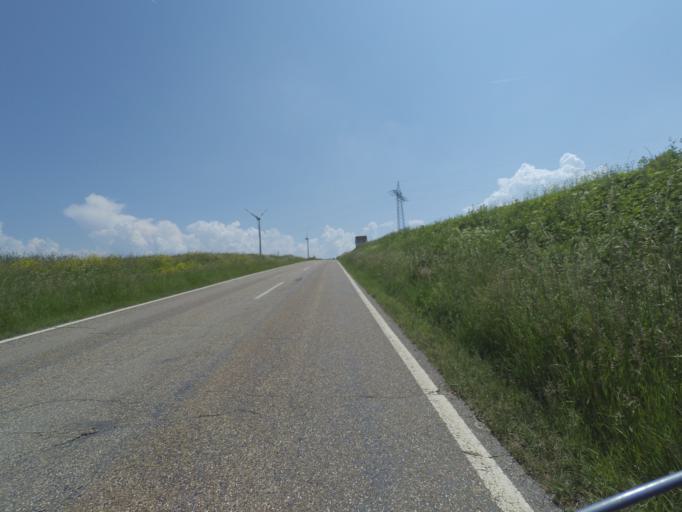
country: DE
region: Rheinland-Pfalz
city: Hambuch
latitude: 50.2386
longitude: 7.1790
